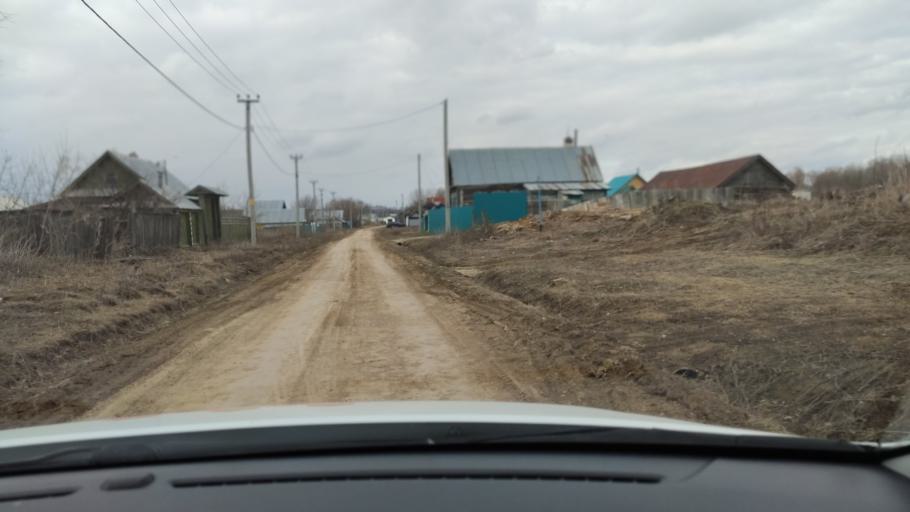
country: RU
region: Tatarstan
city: Vysokaya Gora
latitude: 56.2131
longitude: 49.3131
